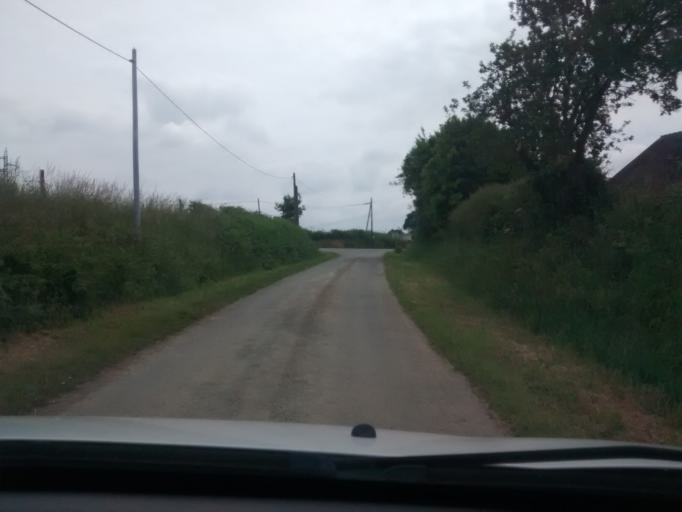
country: FR
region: Brittany
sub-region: Departement d'Ille-et-Vilaine
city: Servon-sur-Vilaine
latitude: 48.1345
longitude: -1.4749
